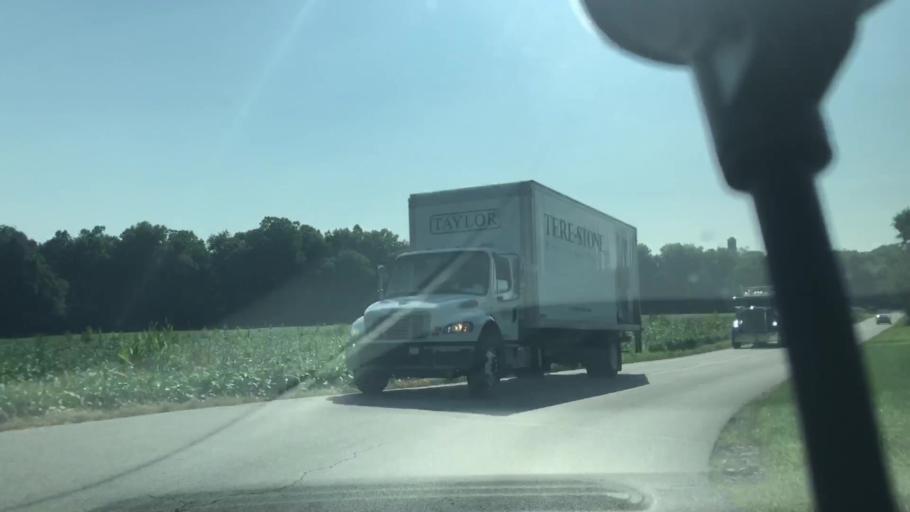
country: US
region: Pennsylvania
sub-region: Montgomery County
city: Sanatoga
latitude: 40.2066
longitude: -75.5850
